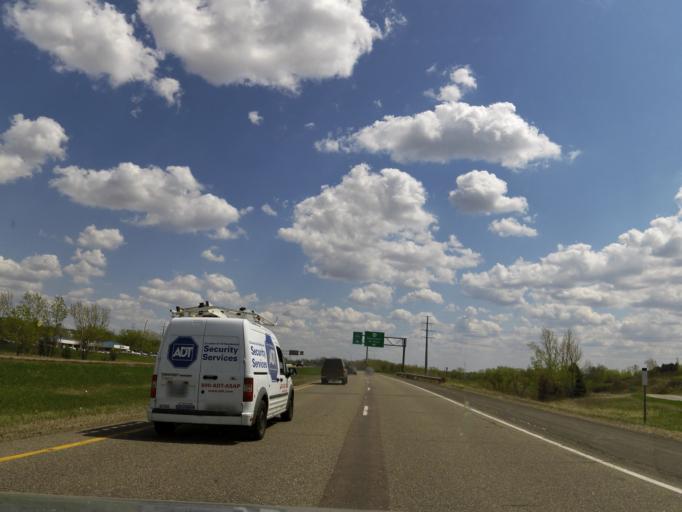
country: US
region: Minnesota
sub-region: Dakota County
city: West Saint Paul
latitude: 44.8791
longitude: -93.0843
